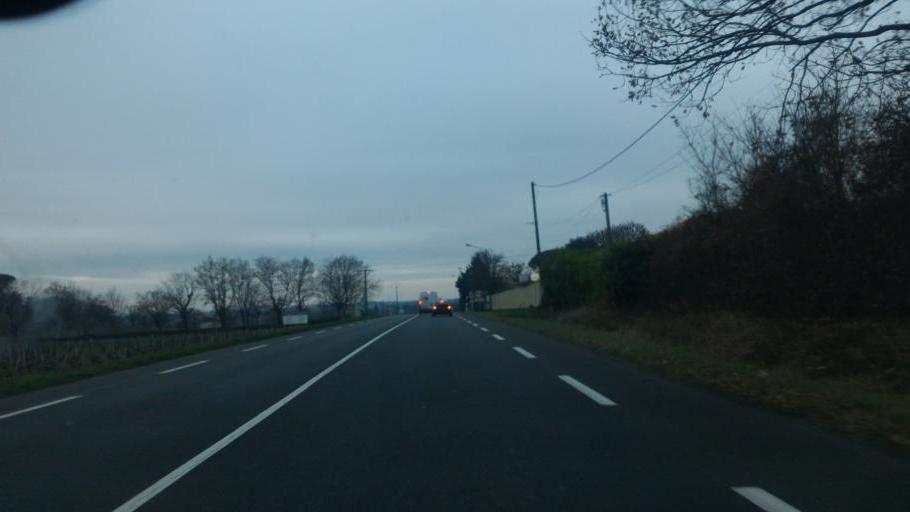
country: FR
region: Aquitaine
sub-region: Departement de la Gironde
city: Cars
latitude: 45.1271
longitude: -0.6174
